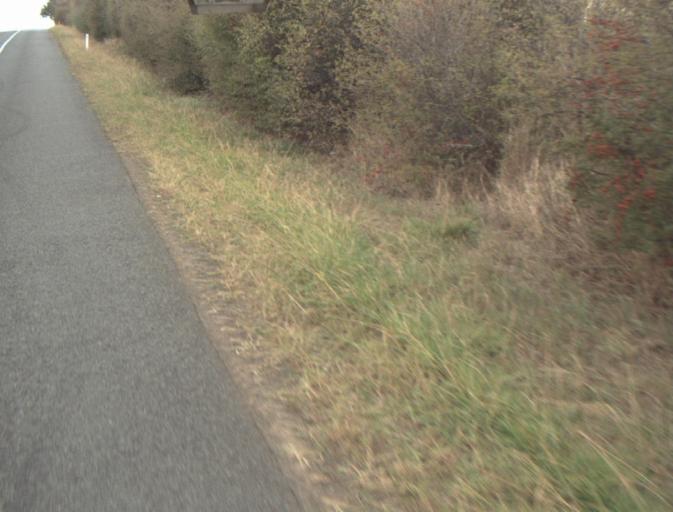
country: AU
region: Tasmania
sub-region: Northern Midlands
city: Evandale
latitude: -41.5145
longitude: 147.2143
